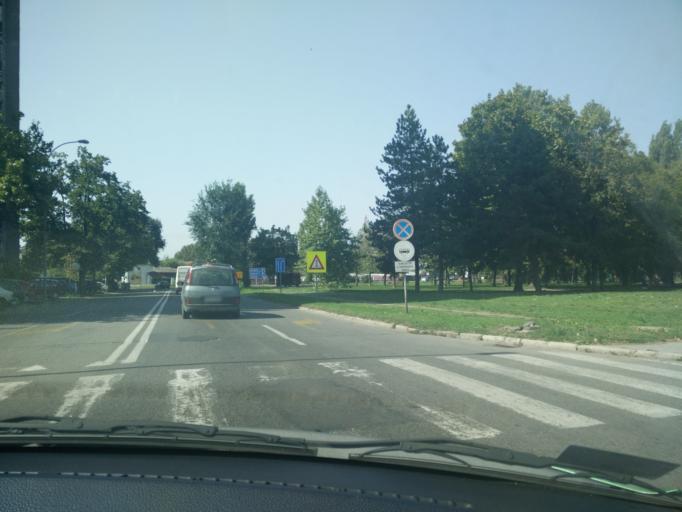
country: RS
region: Autonomna Pokrajina Vojvodina
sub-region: Juznobacki Okrug
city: Novi Sad
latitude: 45.2612
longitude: 19.8560
